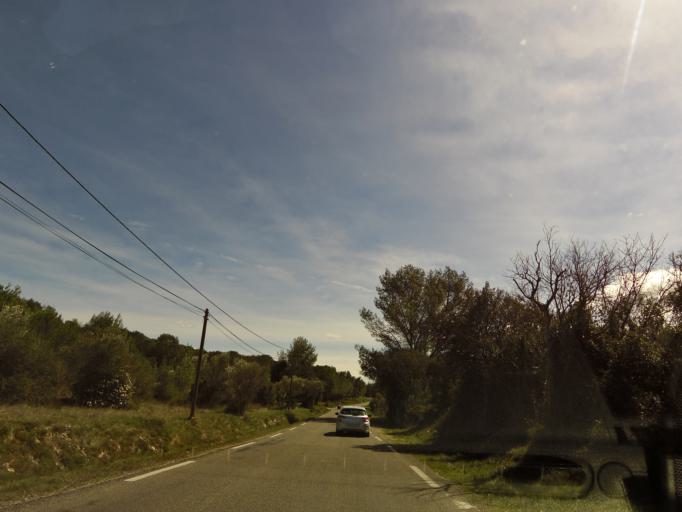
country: FR
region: Languedoc-Roussillon
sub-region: Departement du Gard
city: Bernis
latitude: 43.7815
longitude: 4.2719
